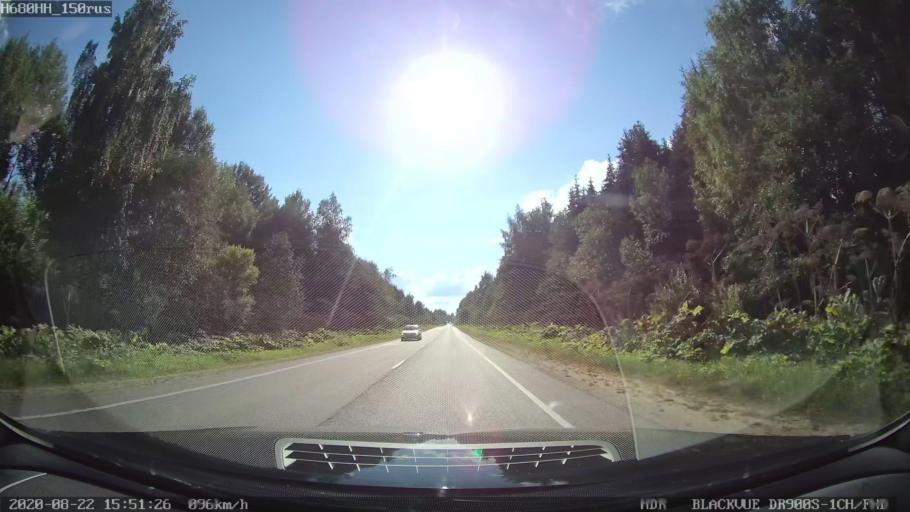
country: RU
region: Tverskaya
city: Bezhetsk
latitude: 57.6648
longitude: 36.4259
